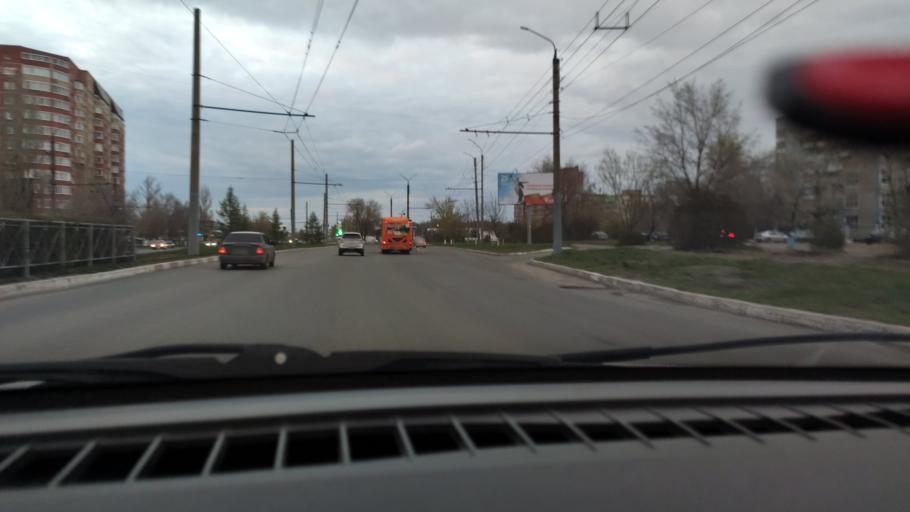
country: RU
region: Orenburg
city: Orenburg
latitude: 51.8162
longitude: 55.1076
